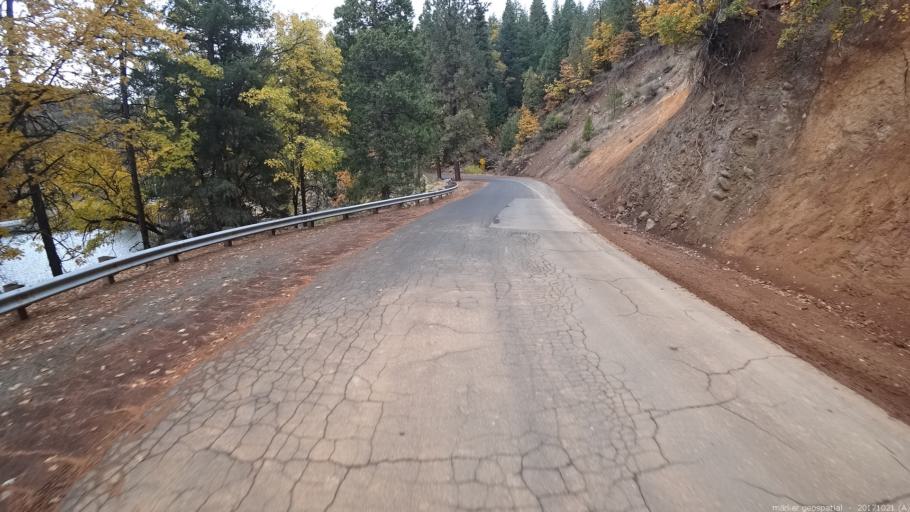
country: US
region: California
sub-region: Shasta County
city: Burney
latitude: 41.0227
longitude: -121.6767
